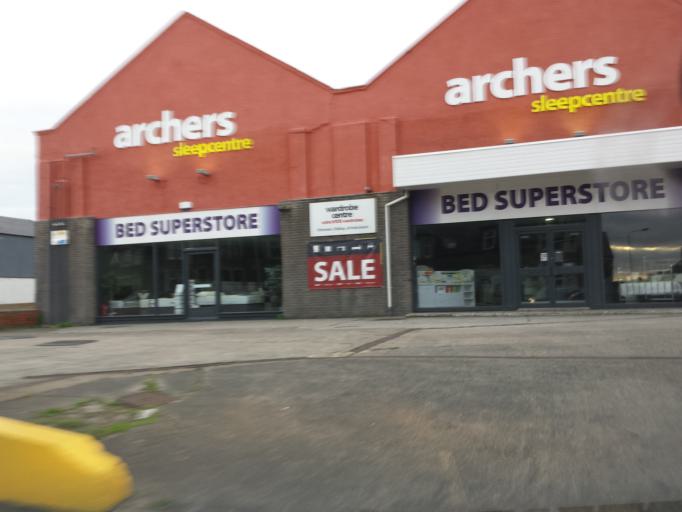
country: GB
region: Scotland
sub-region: South Ayrshire
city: Prestwick
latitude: 55.4773
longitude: -4.6222
